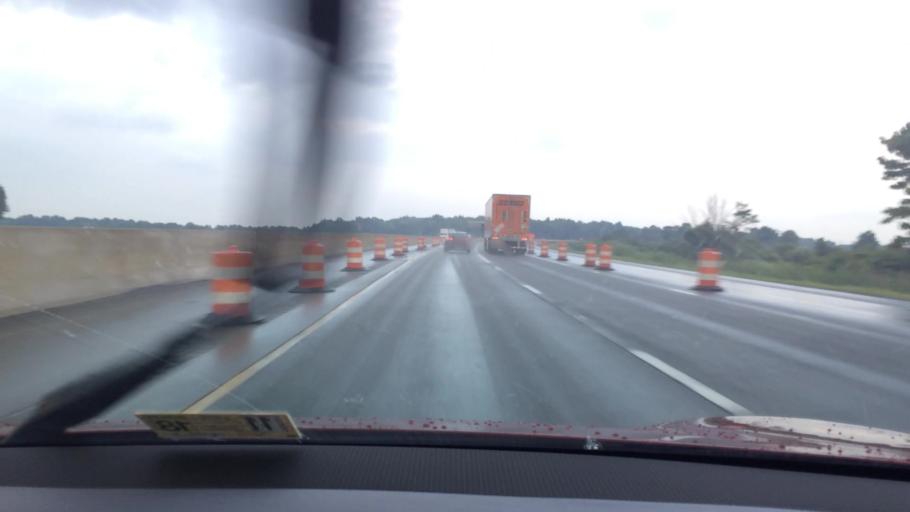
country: US
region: Ohio
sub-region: Lorain County
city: South Amherst
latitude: 41.3664
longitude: -82.2734
